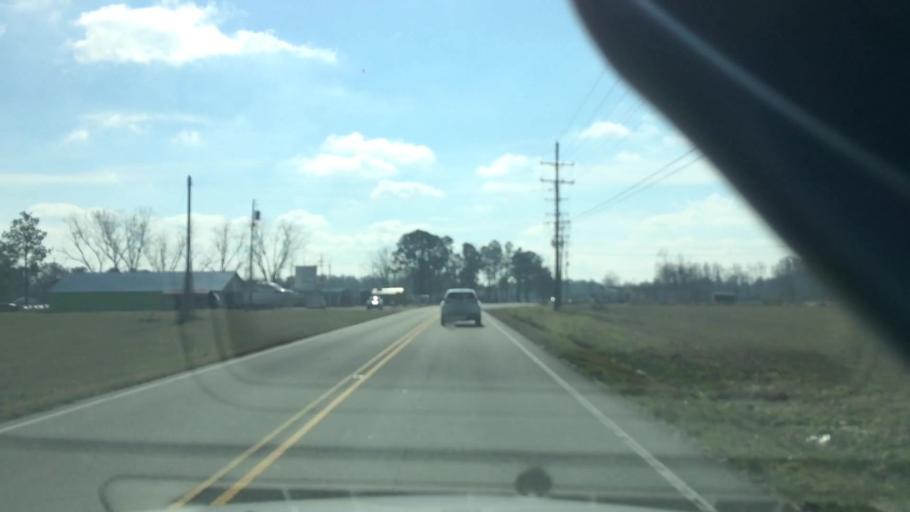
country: US
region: North Carolina
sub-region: Duplin County
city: Beulaville
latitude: 34.8887
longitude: -77.7841
